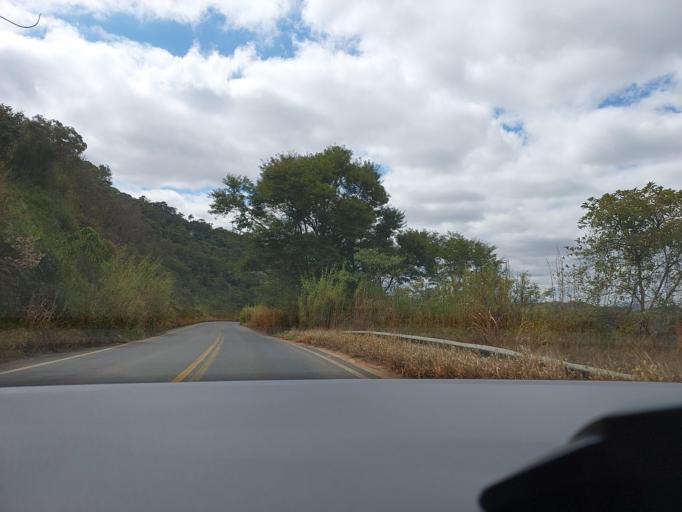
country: BR
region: Minas Gerais
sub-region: Vicosa
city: Vicosa
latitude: -20.8406
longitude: -42.7101
